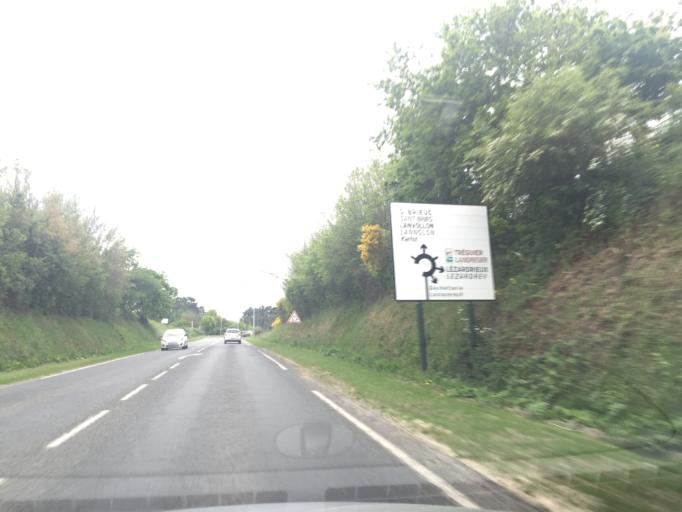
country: FR
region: Brittany
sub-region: Departement des Cotes-d'Armor
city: Paimpol
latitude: 48.7639
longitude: -3.0399
